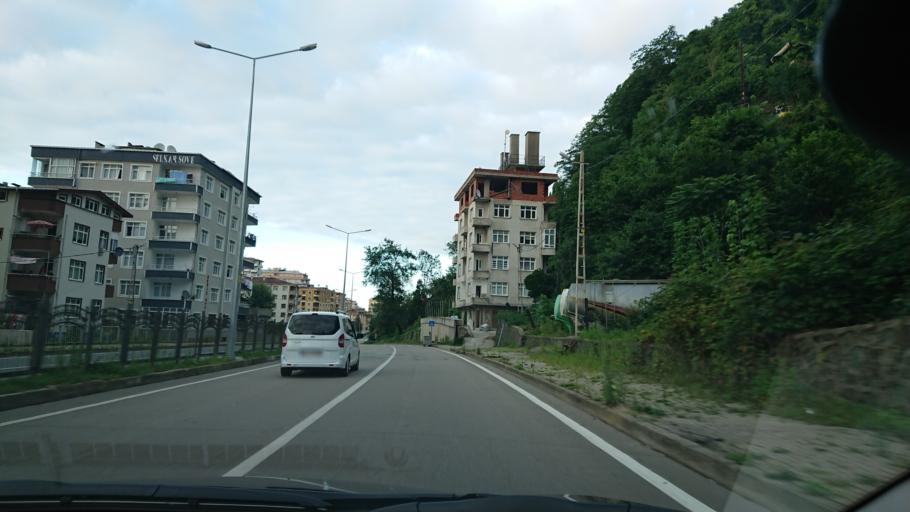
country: TR
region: Rize
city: Rize
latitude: 41.0282
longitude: 40.5555
